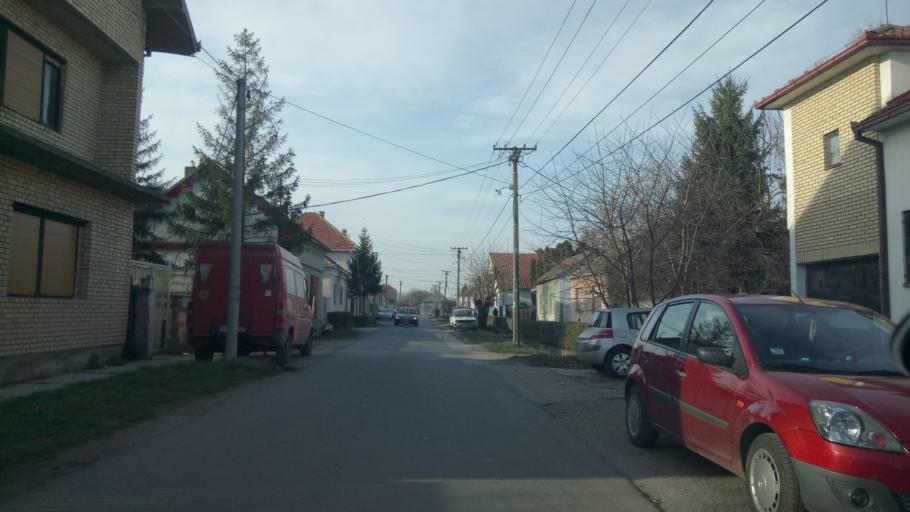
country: RS
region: Autonomna Pokrajina Vojvodina
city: Nova Pazova
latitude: 44.9447
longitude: 20.2228
